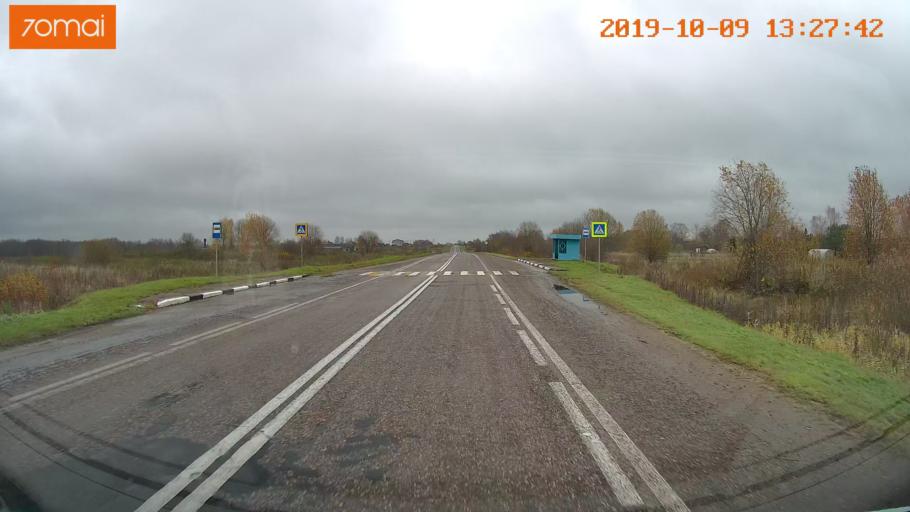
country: RU
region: Jaroslavl
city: Lyubim
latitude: 58.3153
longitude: 40.9525
